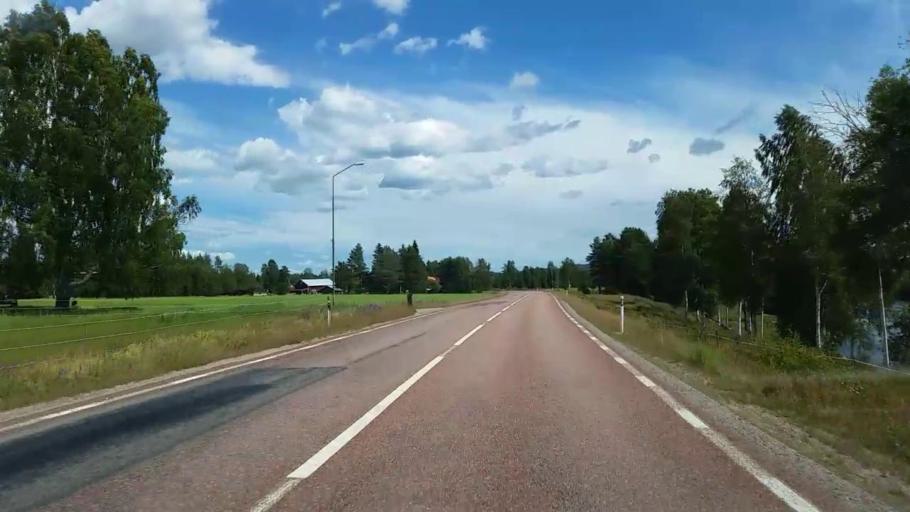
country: SE
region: Gaevleborg
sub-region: Ovanakers Kommun
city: Edsbyn
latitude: 61.3470
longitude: 15.6077
